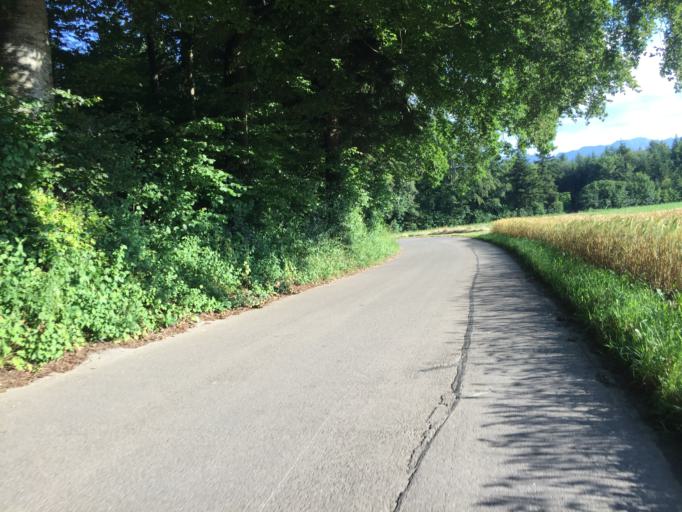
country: CH
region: Bern
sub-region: Bern-Mittelland District
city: Niederwichtrach
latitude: 46.8352
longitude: 7.5835
